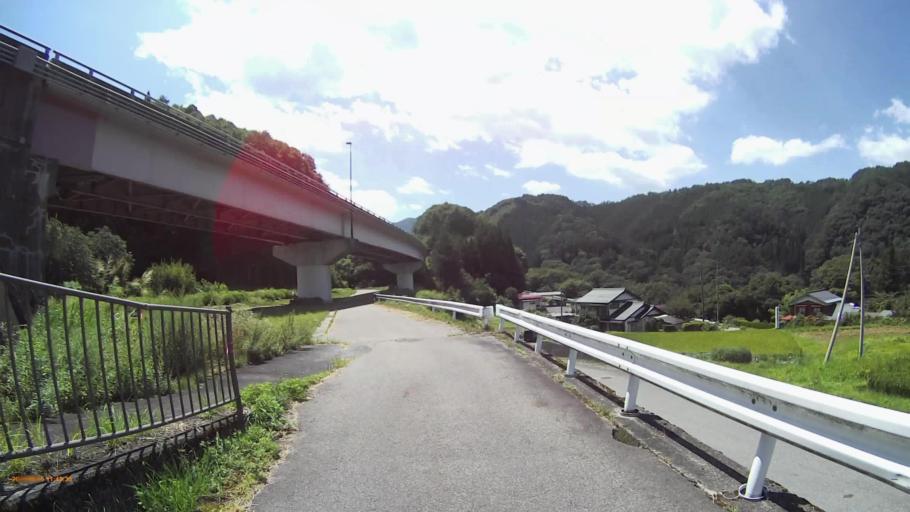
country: JP
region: Nagano
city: Ina
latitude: 35.8321
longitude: 137.6828
